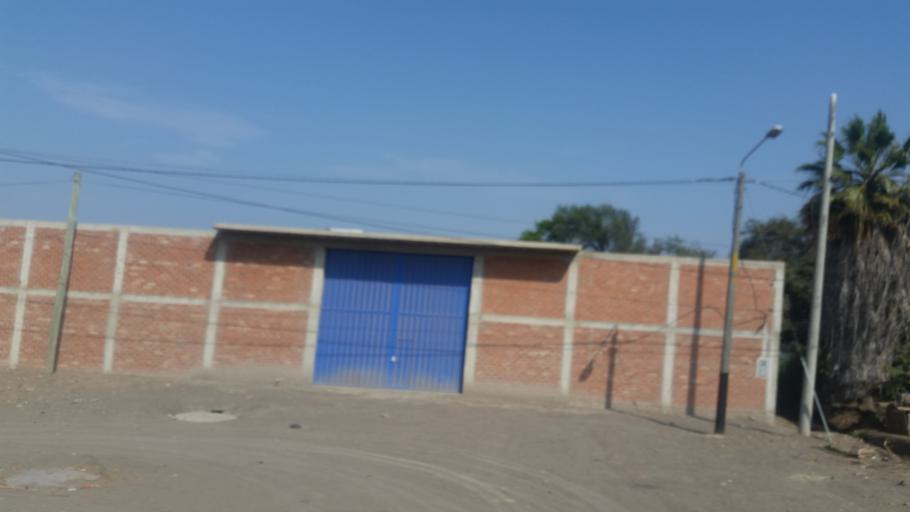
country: PE
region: Lambayeque
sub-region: Provincia de Chiclayo
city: Chiclayo
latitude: -6.8109
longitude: -79.8294
